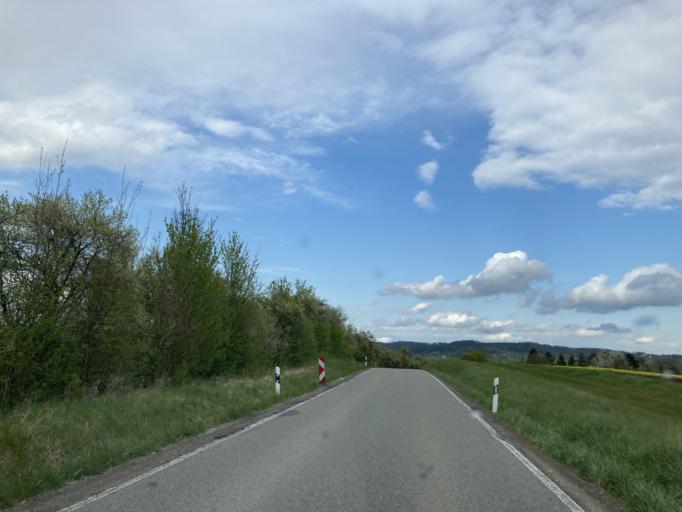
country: DE
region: Baden-Wuerttemberg
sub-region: Tuebingen Region
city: Rottenburg
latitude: 48.5308
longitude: 8.9369
